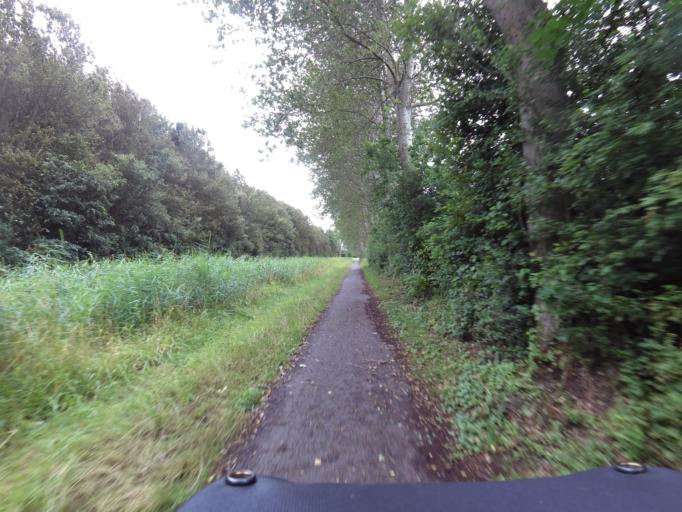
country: NL
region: South Holland
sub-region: Gemeente Goeree-Overflakkee
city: Goedereede
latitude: 51.8298
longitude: 4.0021
